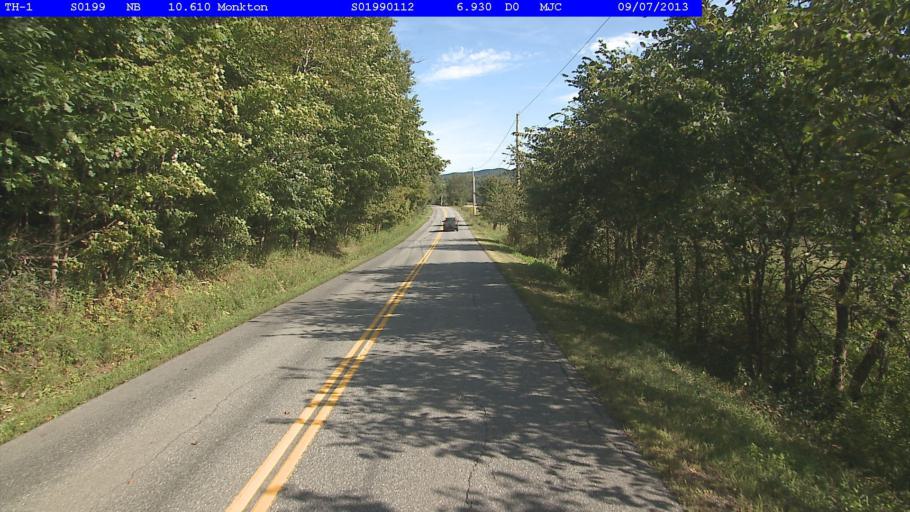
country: US
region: Vermont
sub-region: Chittenden County
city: Hinesburg
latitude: 44.2763
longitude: -73.1102
